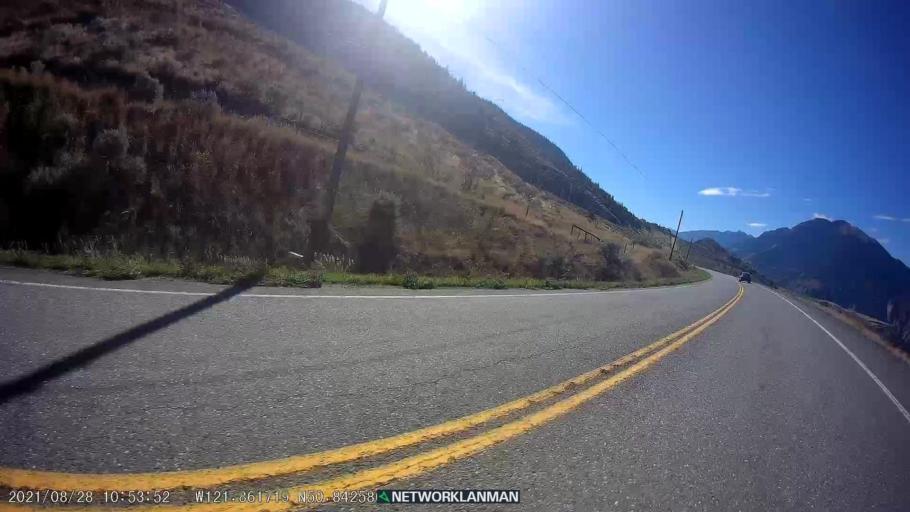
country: CA
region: British Columbia
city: Lillooet
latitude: 50.8452
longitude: -121.8629
